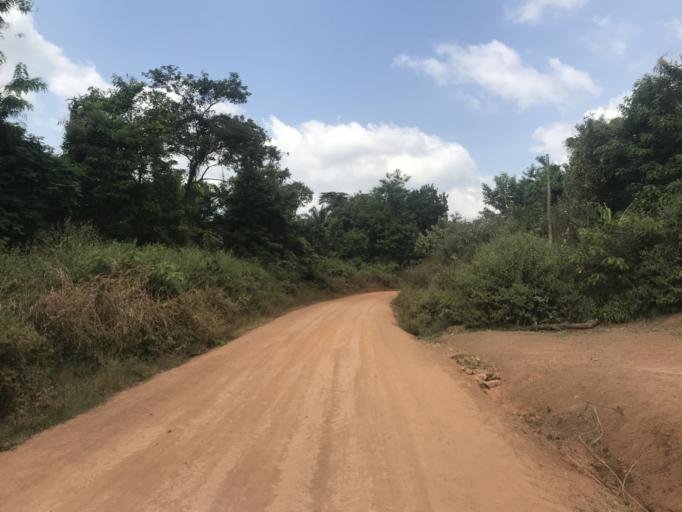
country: NG
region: Osun
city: Inisa
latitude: 7.8586
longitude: 4.3819
